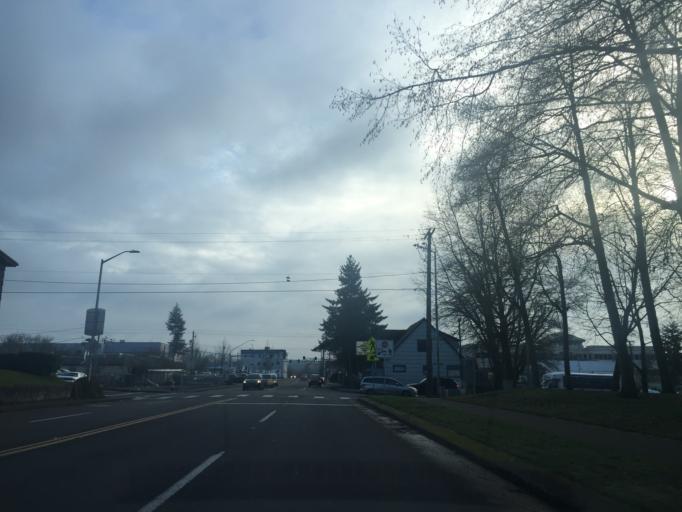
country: US
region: Washington
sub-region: Thurston County
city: Olympia
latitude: 47.0478
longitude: -122.8932
